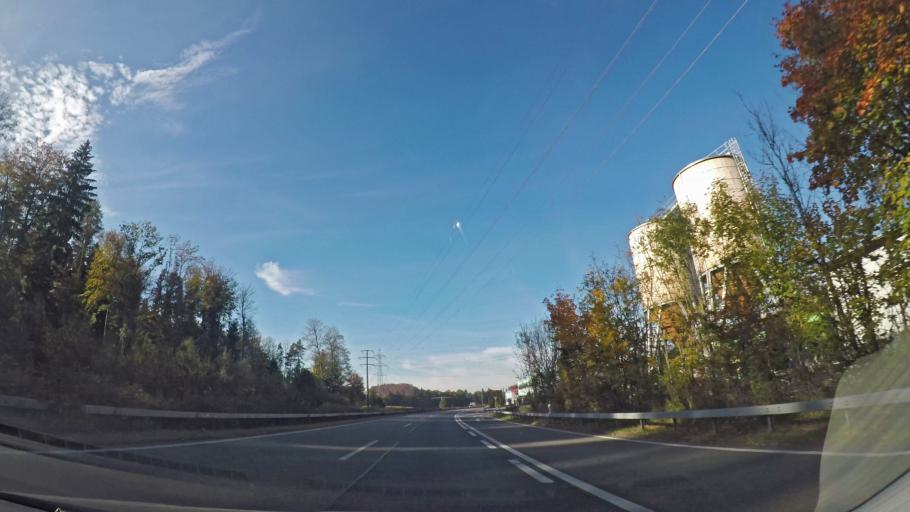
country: CH
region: Bern
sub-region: Frutigen-Niedersimmental District
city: Wimmis
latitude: 46.6977
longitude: 7.6398
